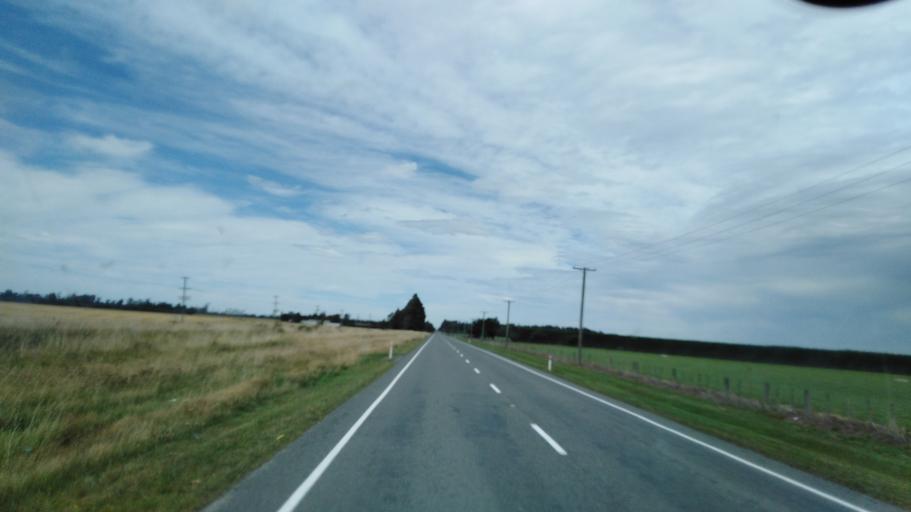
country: NZ
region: Canterbury
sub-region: Selwyn District
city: Darfield
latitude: -43.4280
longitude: 172.0550
